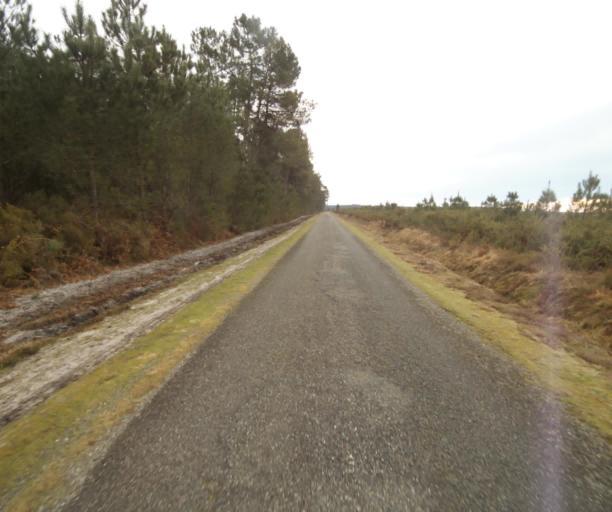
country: FR
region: Aquitaine
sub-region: Departement des Landes
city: Gabarret
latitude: 44.0712
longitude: -0.0166
